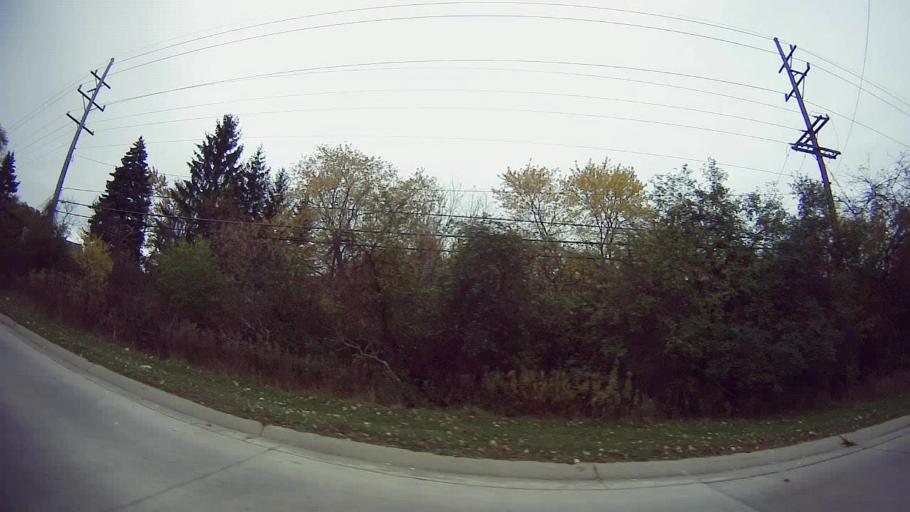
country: US
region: Michigan
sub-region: Oakland County
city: Sylvan Lake
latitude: 42.6168
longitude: -83.3165
